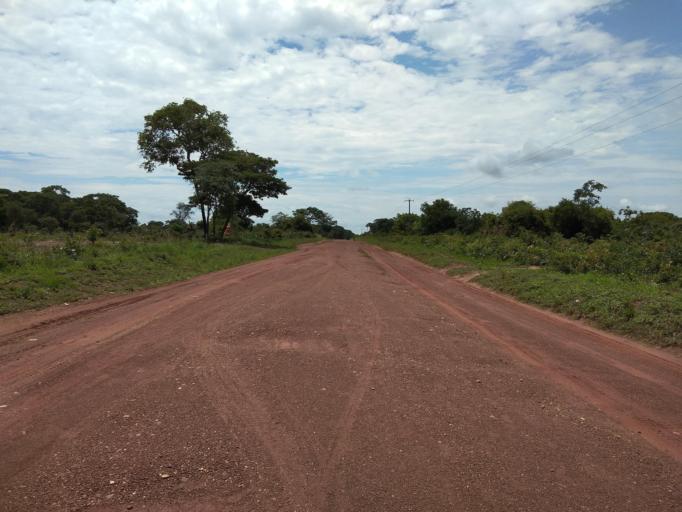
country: ZM
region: Copperbelt
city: Luanshya
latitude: -13.4817
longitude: 28.7648
